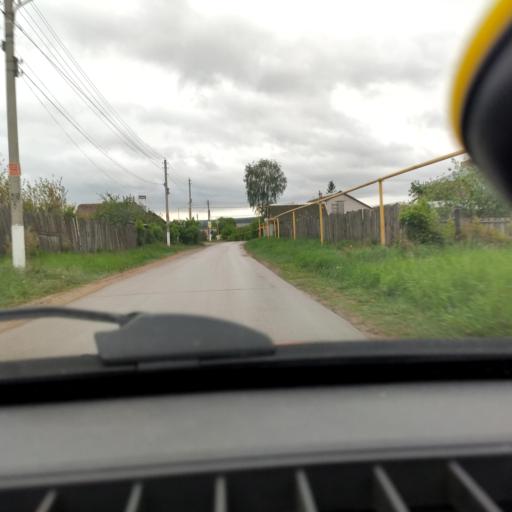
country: RU
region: Samara
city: Zhigulevsk
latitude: 53.5540
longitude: 49.5345
